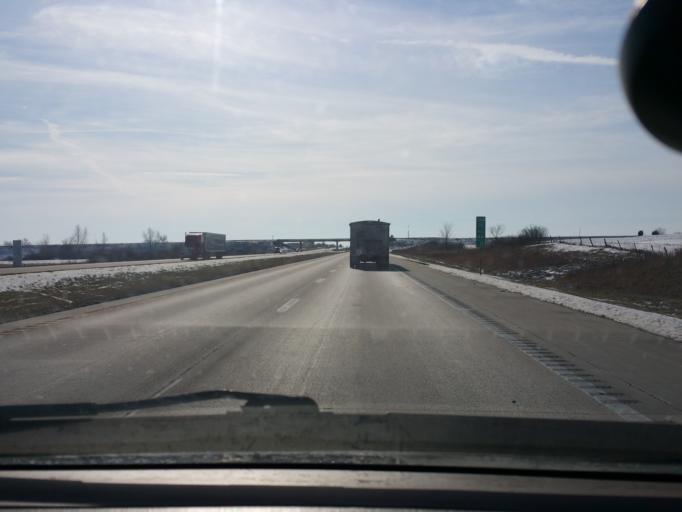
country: US
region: Missouri
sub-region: Clinton County
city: Cameron
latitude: 39.6365
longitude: -94.2437
